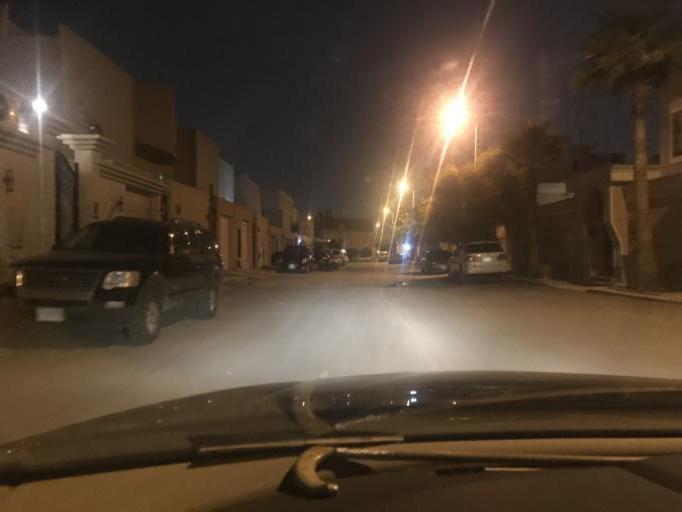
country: SA
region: Ar Riyad
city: Riyadh
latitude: 24.7510
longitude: 46.7763
